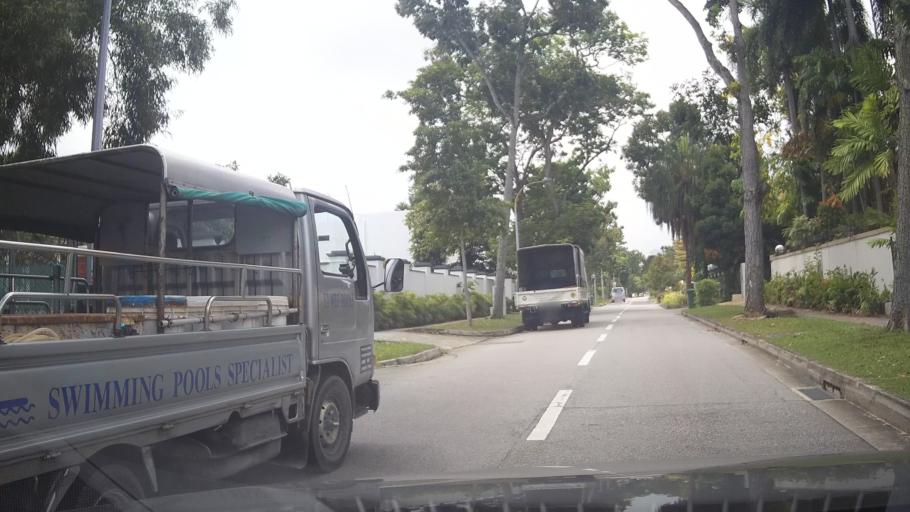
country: SG
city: Singapore
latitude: 1.3027
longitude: 103.8919
